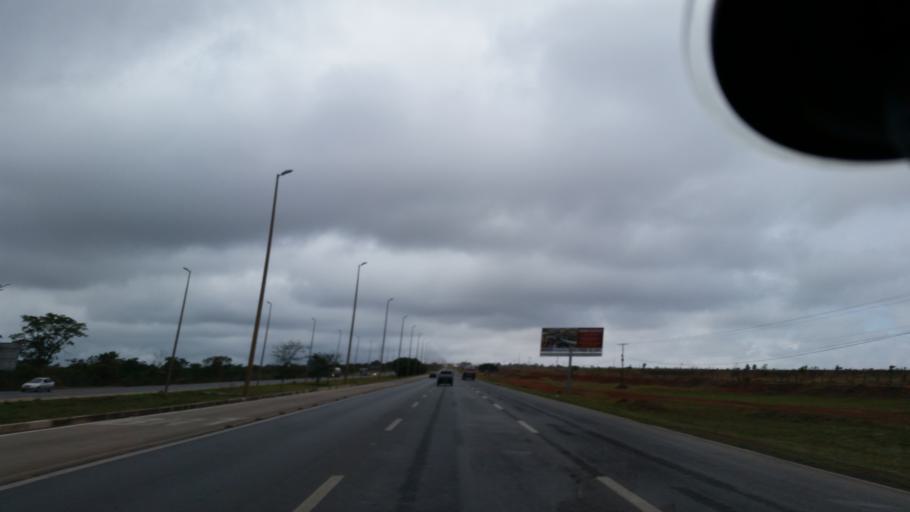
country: BR
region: Federal District
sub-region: Brasilia
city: Brasilia
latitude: -15.9555
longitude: -47.9943
